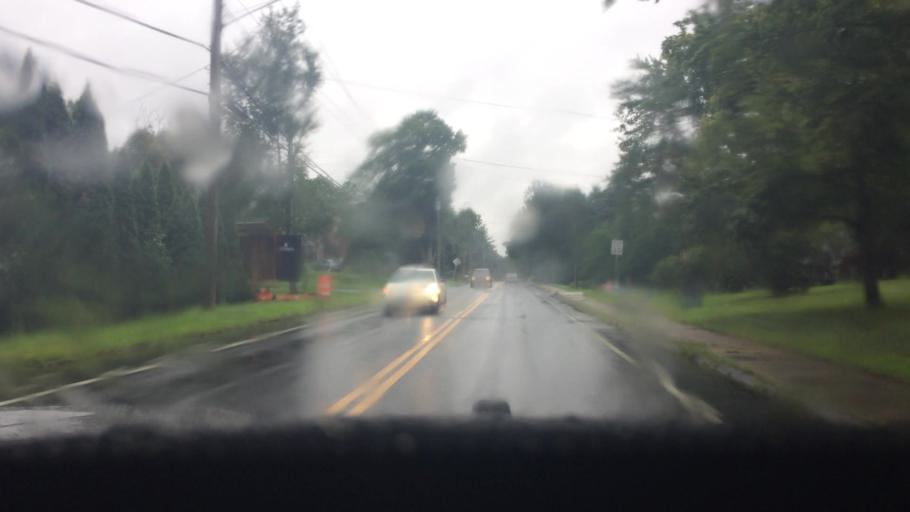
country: US
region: Connecticut
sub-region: Hartford County
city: Blue Hills
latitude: 41.8381
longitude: -72.7335
